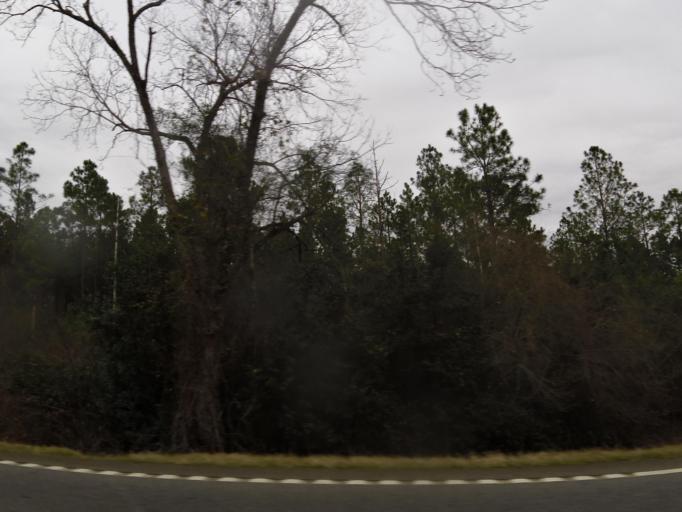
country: US
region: Georgia
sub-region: Randolph County
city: Shellman
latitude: 31.7776
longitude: -84.5763
